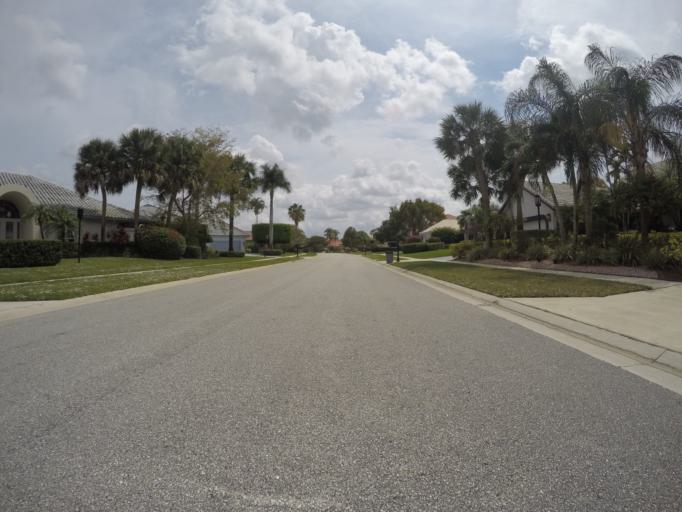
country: US
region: Florida
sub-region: Palm Beach County
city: Villages of Oriole
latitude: 26.4106
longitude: -80.2131
